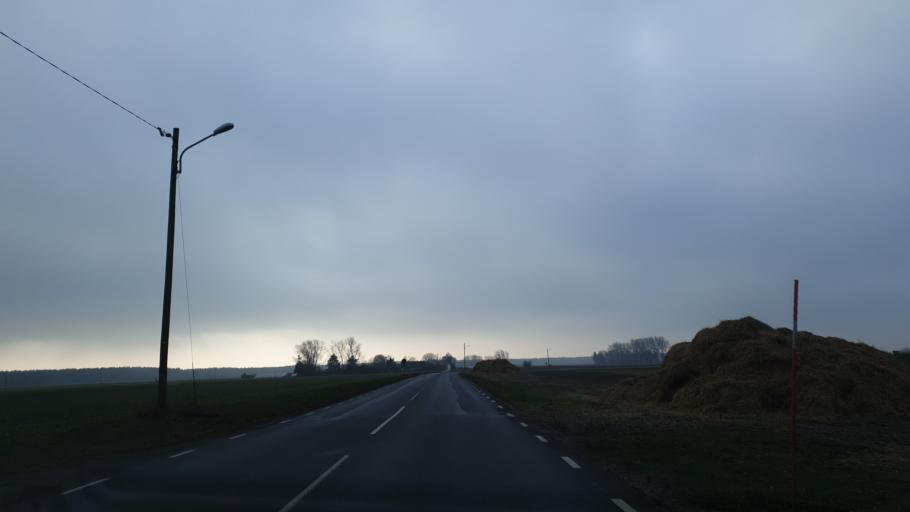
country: SE
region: Skane
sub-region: Kristianstads Kommun
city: Fjalkinge
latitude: 55.9951
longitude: 14.3487
